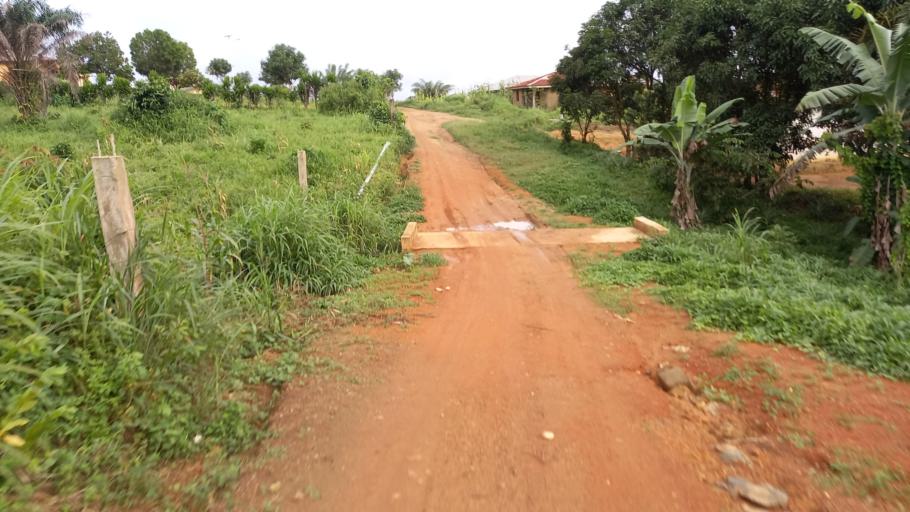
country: SL
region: Eastern Province
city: Kailahun
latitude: 8.2725
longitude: -10.5817
